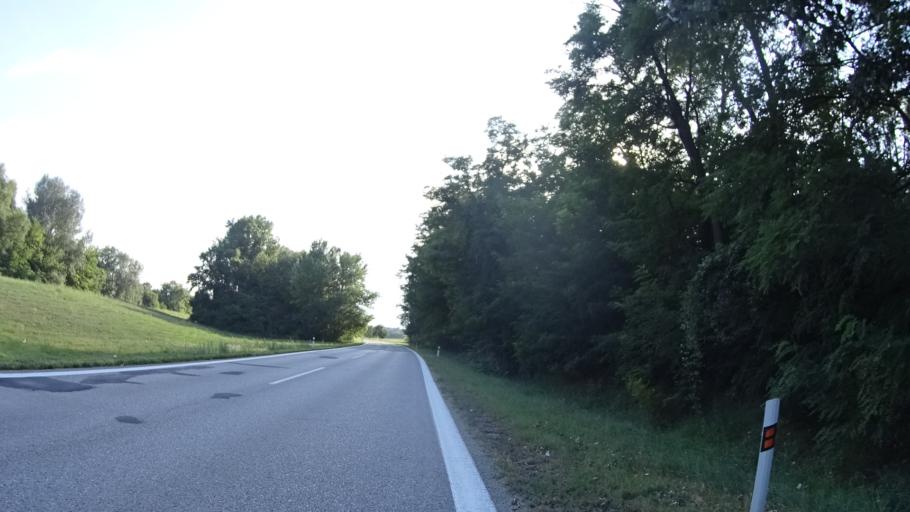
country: HU
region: Komarom-Esztergom
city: Nyergesujfalu
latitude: 47.7726
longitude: 18.5457
